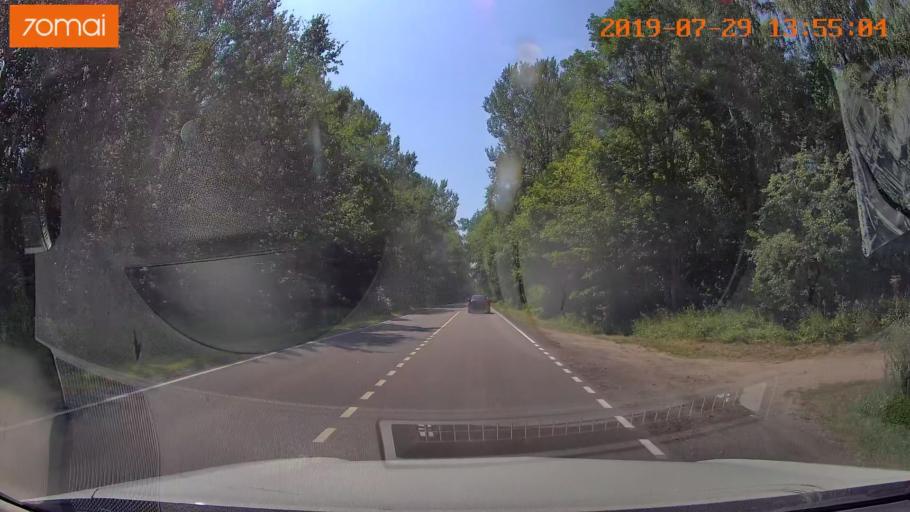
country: RU
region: Kaliningrad
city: Primorsk
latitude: 54.7182
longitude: 19.9606
